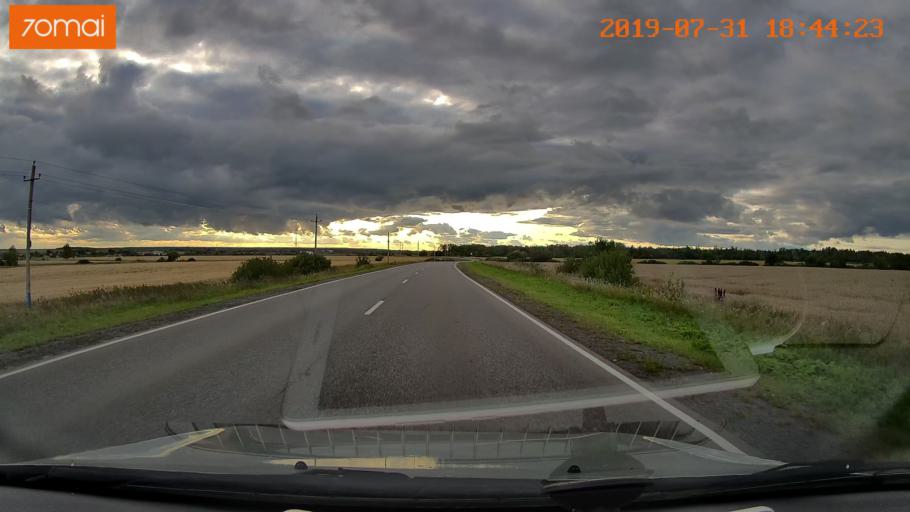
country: RU
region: Moskovskaya
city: Troitskoye
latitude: 55.2494
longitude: 38.5525
